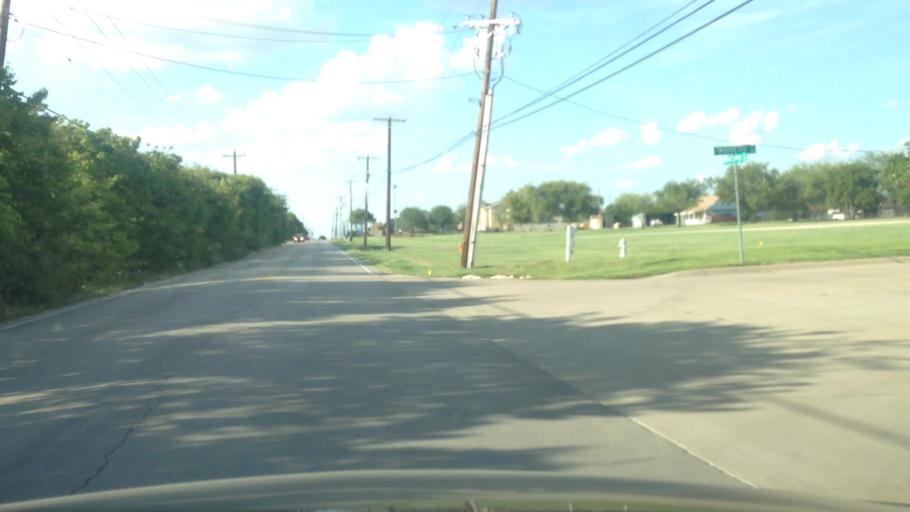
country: US
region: Texas
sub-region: Tarrant County
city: Haslet
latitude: 32.9341
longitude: -97.3920
